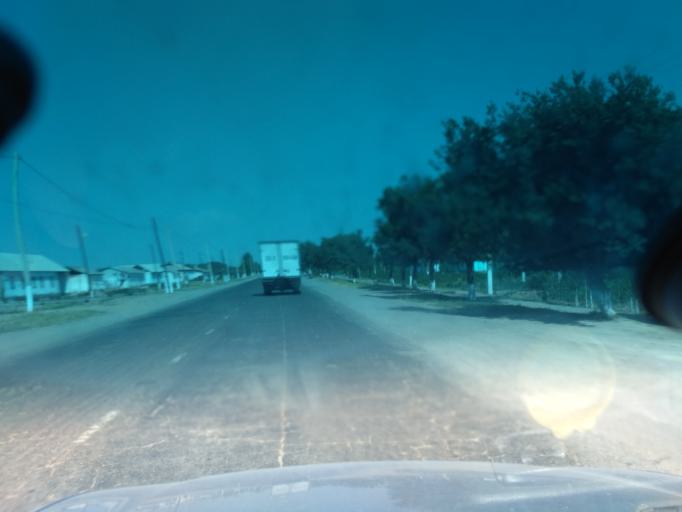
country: UZ
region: Sirdaryo
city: Guliston
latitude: 40.4877
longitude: 68.8812
